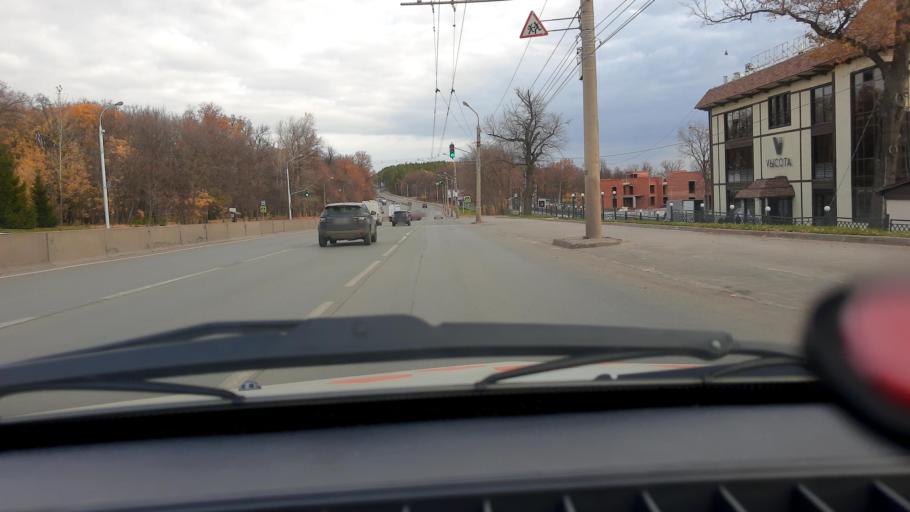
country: RU
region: Bashkortostan
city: Ufa
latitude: 54.7306
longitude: 56.0247
